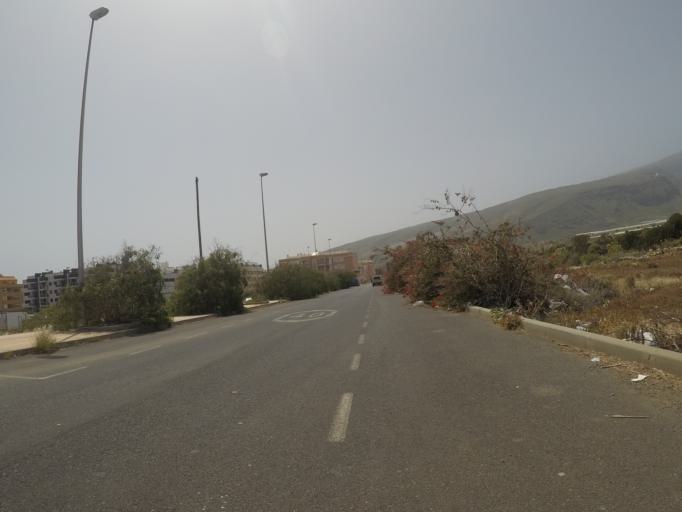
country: ES
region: Canary Islands
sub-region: Provincia de Santa Cruz de Tenerife
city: Candelaria
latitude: 28.2981
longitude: -16.3747
